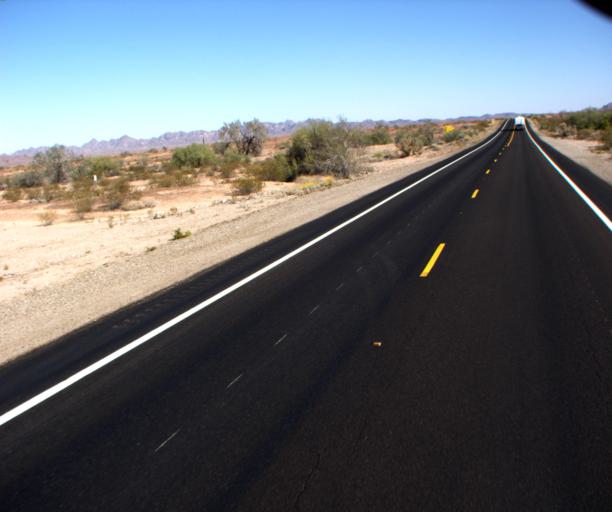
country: US
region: Arizona
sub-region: Yuma County
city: Wellton
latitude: 33.1211
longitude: -114.2920
